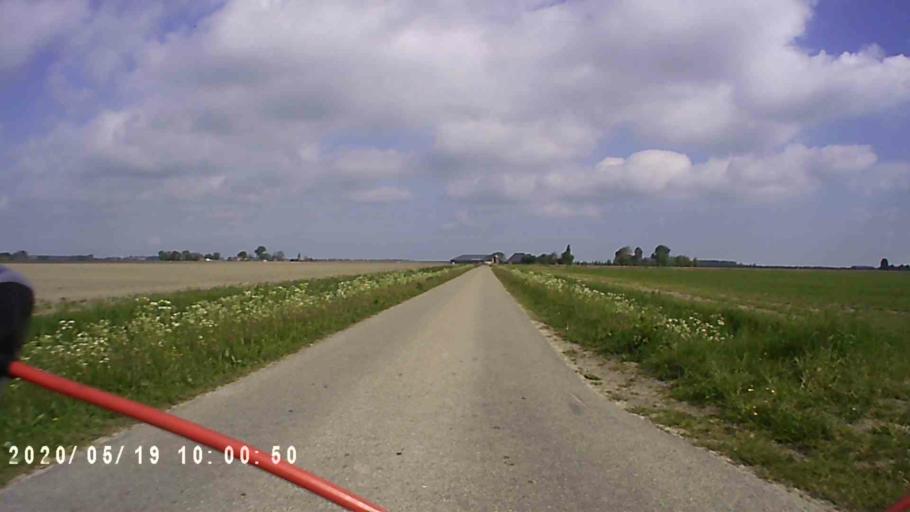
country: NL
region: Groningen
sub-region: Gemeente Zuidhorn
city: Grijpskerk
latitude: 53.3000
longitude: 6.2365
